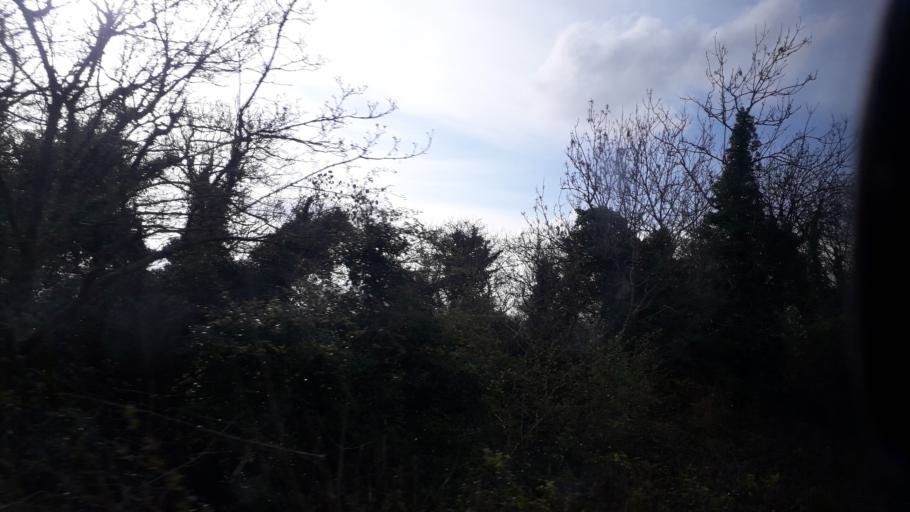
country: IE
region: Leinster
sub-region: An Mhi
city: Longwood
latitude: 53.4522
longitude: -6.9580
